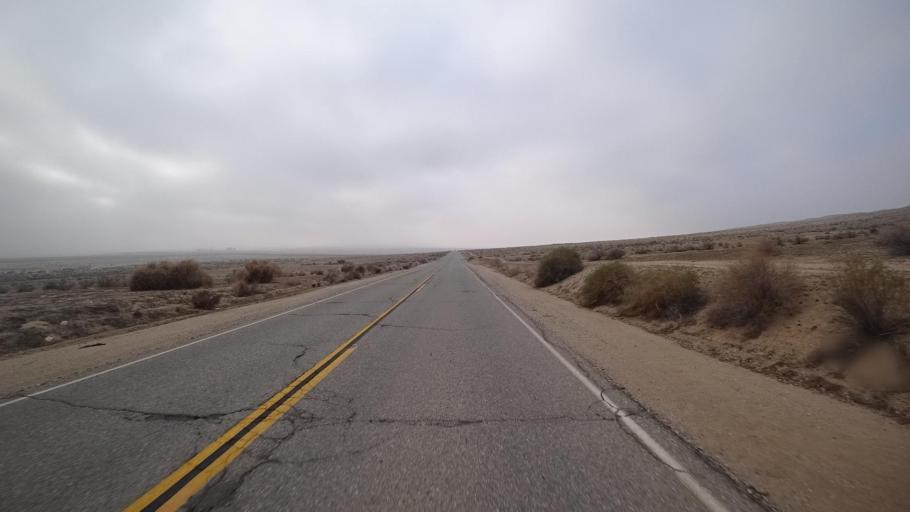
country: US
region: California
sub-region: Kern County
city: Maricopa
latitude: 35.1301
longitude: -119.3804
